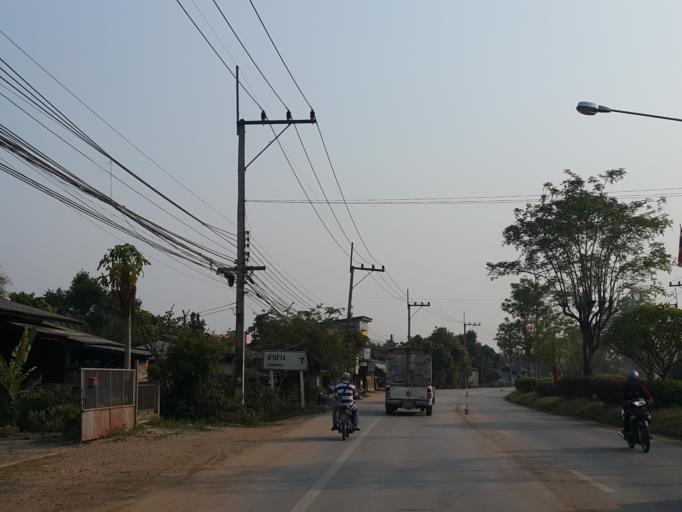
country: TH
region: Lampang
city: Lampang
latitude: 18.3411
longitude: 99.5347
